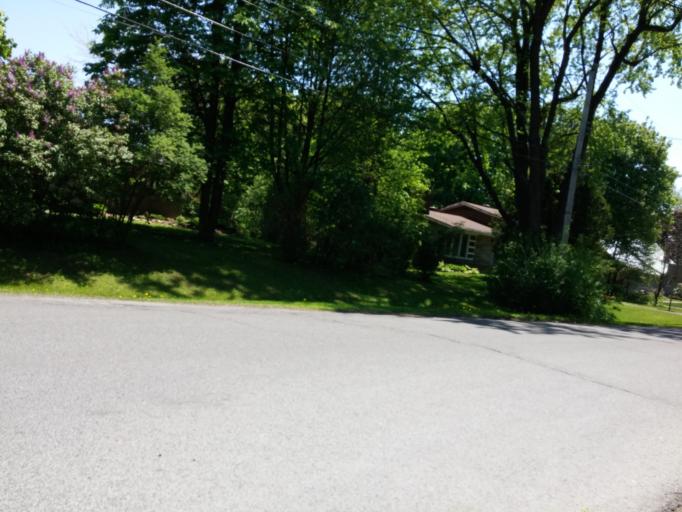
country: CA
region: Quebec
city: Baie-D'Urfe
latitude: 45.4204
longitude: -73.8980
